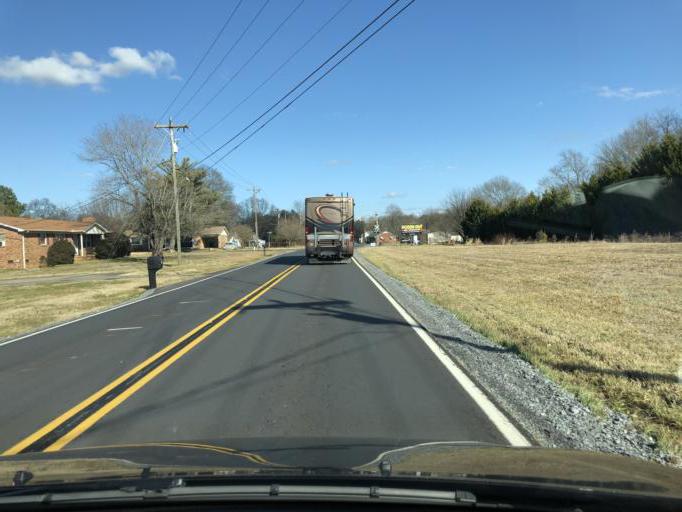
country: US
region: North Carolina
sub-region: Cleveland County
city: Shelby
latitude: 35.2285
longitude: -81.5210
